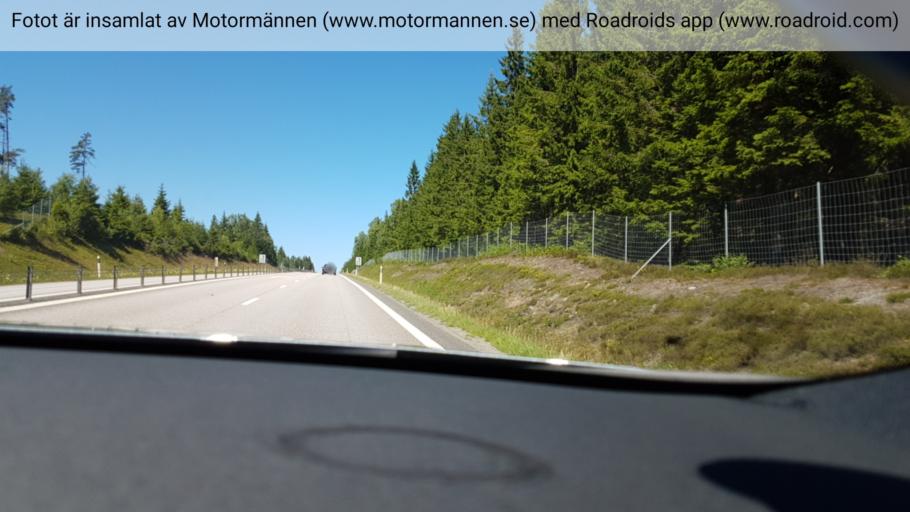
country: SE
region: Vaestra Goetaland
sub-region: Ulricehamns Kommun
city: Ulricehamn
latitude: 57.7846
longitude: 13.6464
